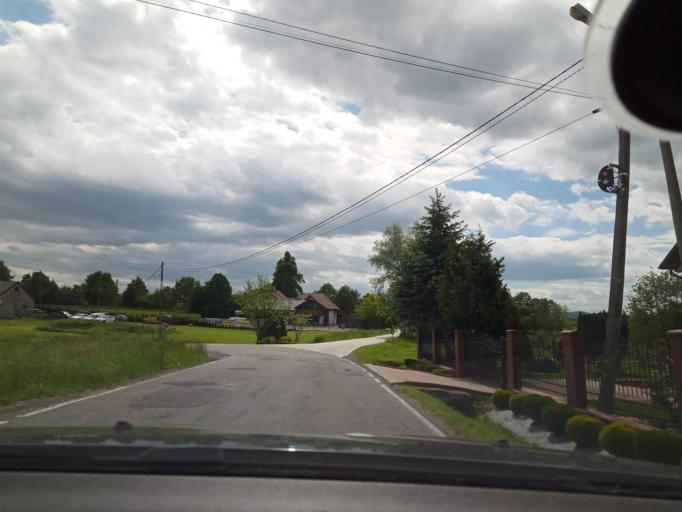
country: PL
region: Lesser Poland Voivodeship
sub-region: Powiat bochenski
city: Lapanow
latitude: 49.8560
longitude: 20.2515
